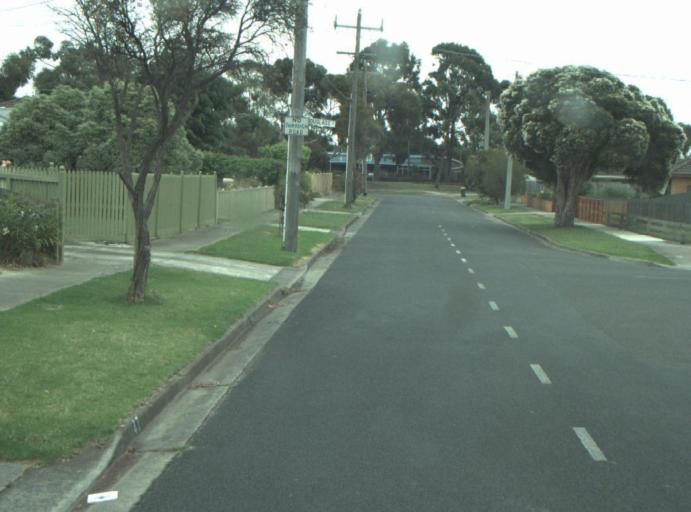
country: AU
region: Victoria
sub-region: Greater Geelong
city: Hamlyn Heights
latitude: -38.1321
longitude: 144.3250
